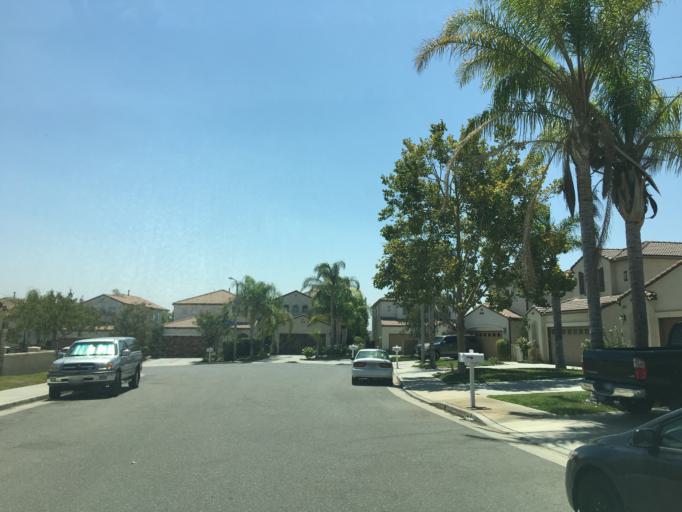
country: US
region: California
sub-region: Los Angeles County
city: Castaic
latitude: 34.5018
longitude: -118.6207
